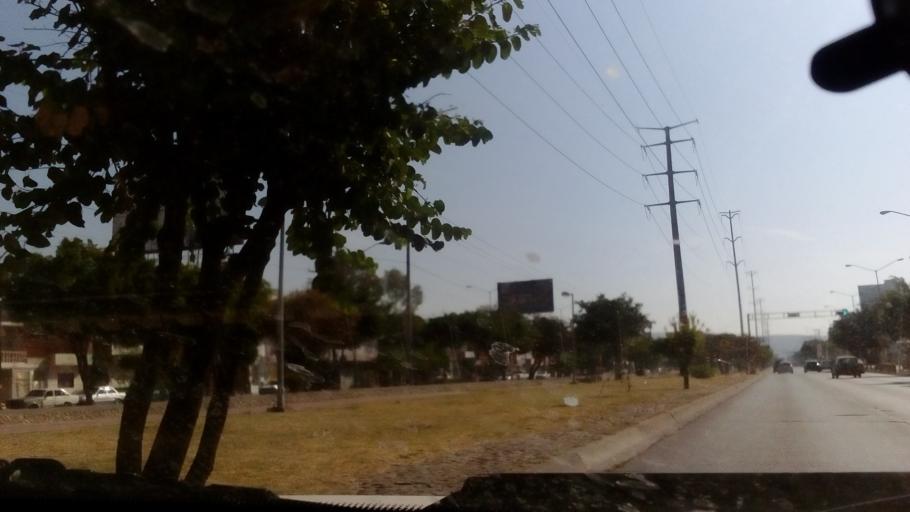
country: MX
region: Guanajuato
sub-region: Leon
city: Medina
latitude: 21.1436
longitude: -101.6413
